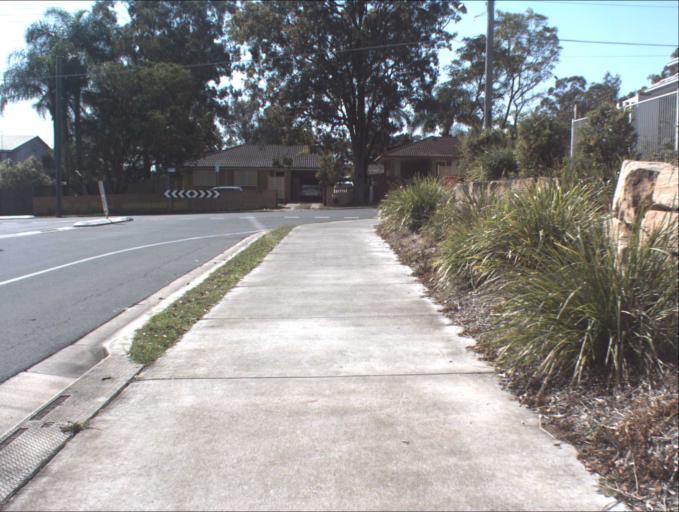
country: AU
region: Queensland
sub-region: Logan
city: Logan City
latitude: -27.6748
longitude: 153.0938
